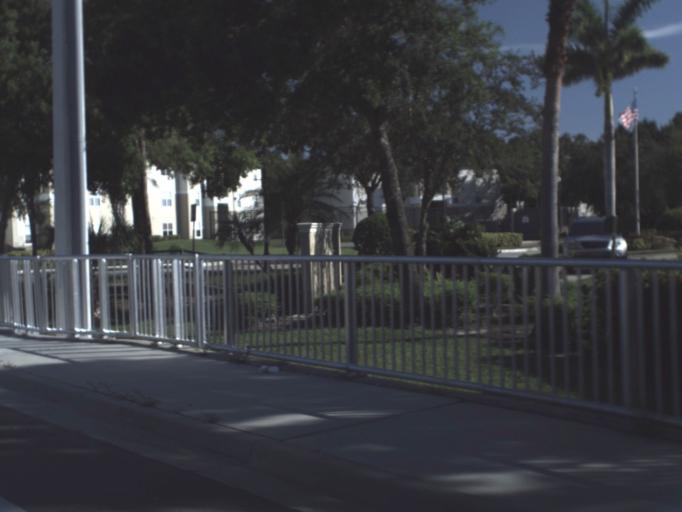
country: US
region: Florida
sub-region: Lee County
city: Fort Myers
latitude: 26.6078
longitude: -81.8507
